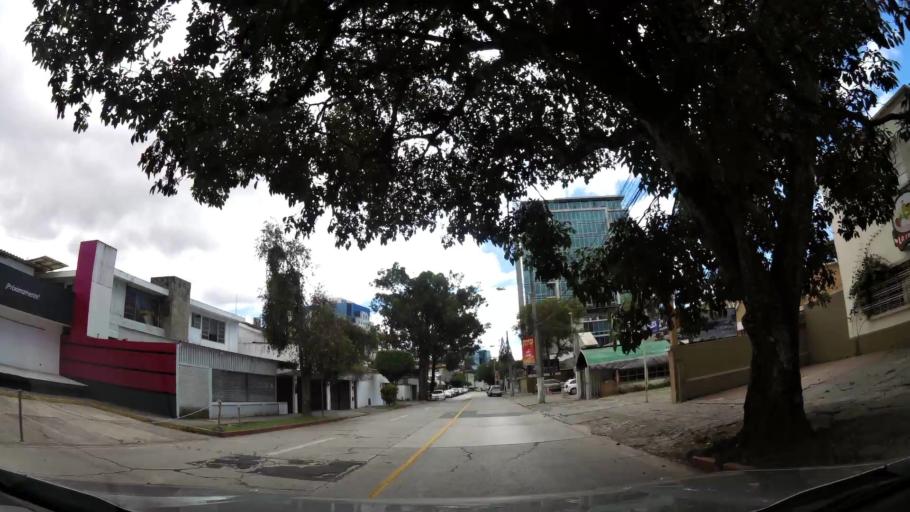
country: GT
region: Guatemala
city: Santa Catarina Pinula
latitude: 14.5948
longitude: -90.5126
